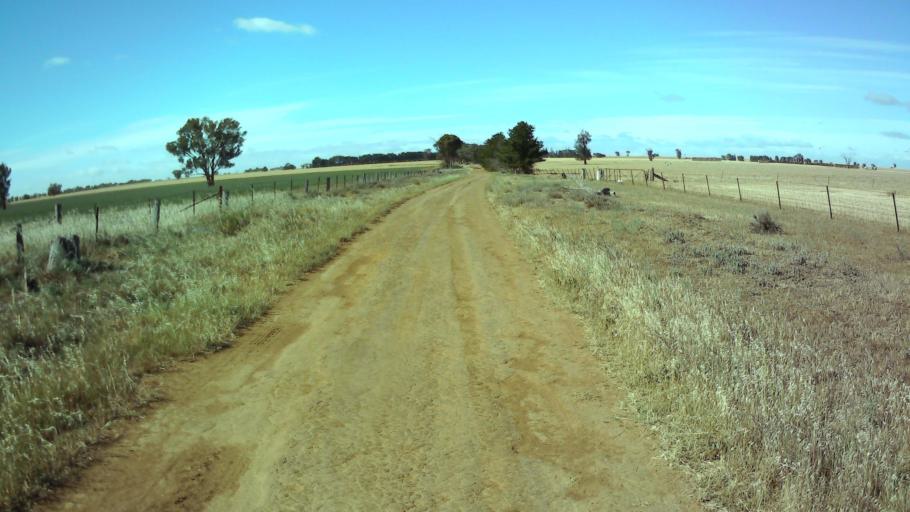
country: AU
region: New South Wales
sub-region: Weddin
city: Grenfell
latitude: -34.0497
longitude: 148.2692
